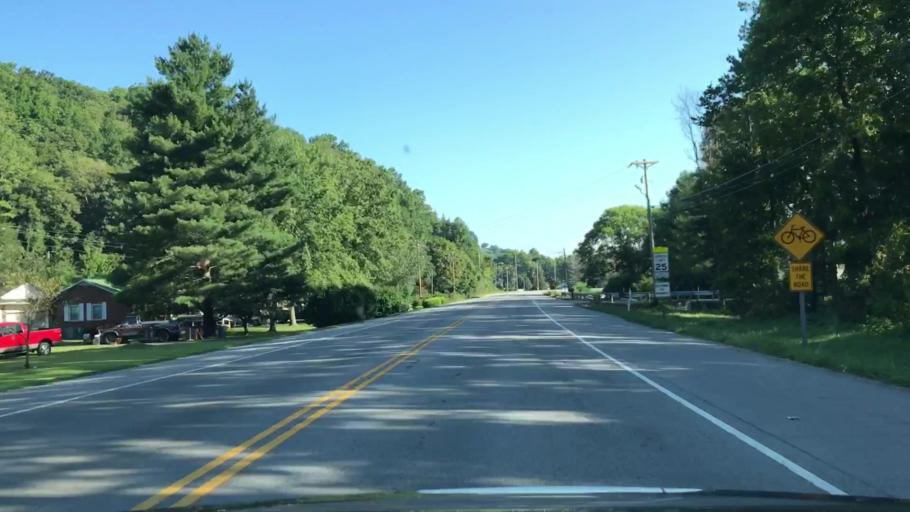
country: US
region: Tennessee
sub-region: Jackson County
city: Gainesboro
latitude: 36.3460
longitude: -85.6582
